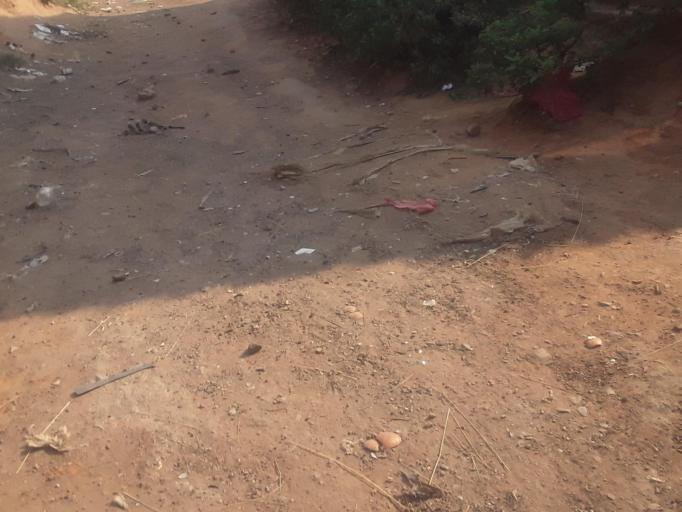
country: ZM
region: Lusaka
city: Lusaka
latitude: -15.3577
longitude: 28.2910
